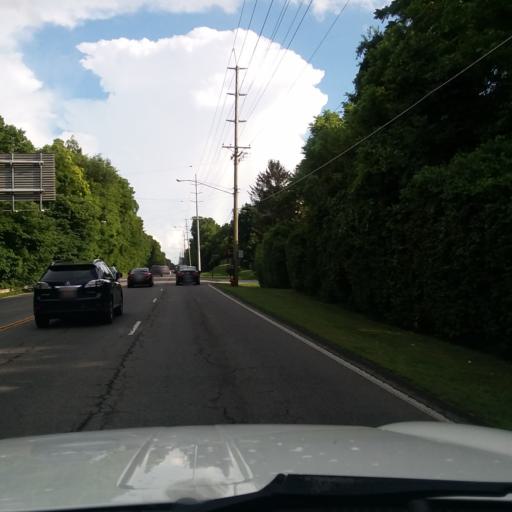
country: US
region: Tennessee
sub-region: Davidson County
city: Oak Hill
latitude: 36.1041
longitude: -86.7727
